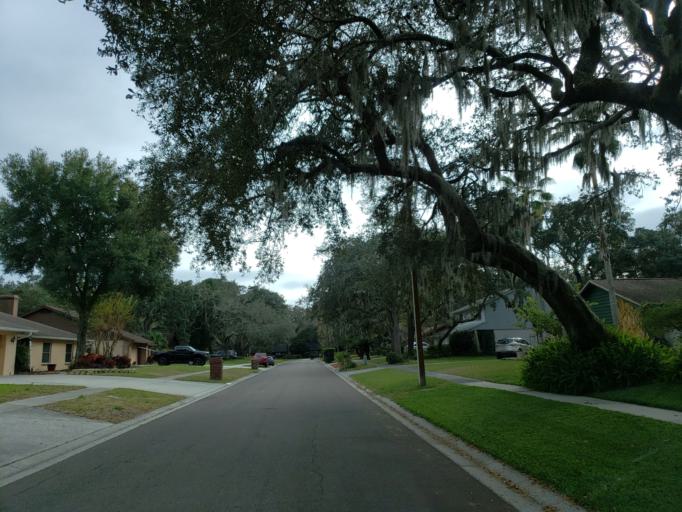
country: US
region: Florida
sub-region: Hillsborough County
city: Riverview
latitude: 27.8827
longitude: -82.2851
